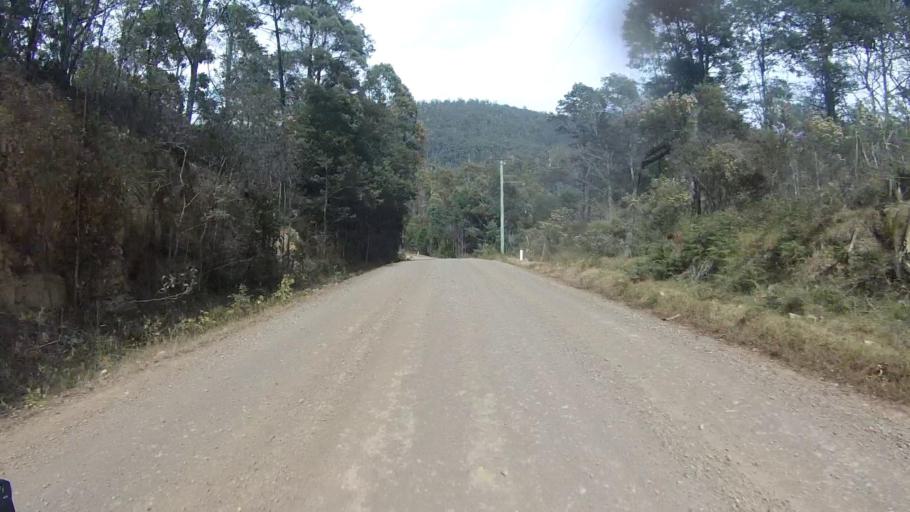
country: AU
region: Tasmania
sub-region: Sorell
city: Sorell
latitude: -42.6894
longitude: 147.8674
